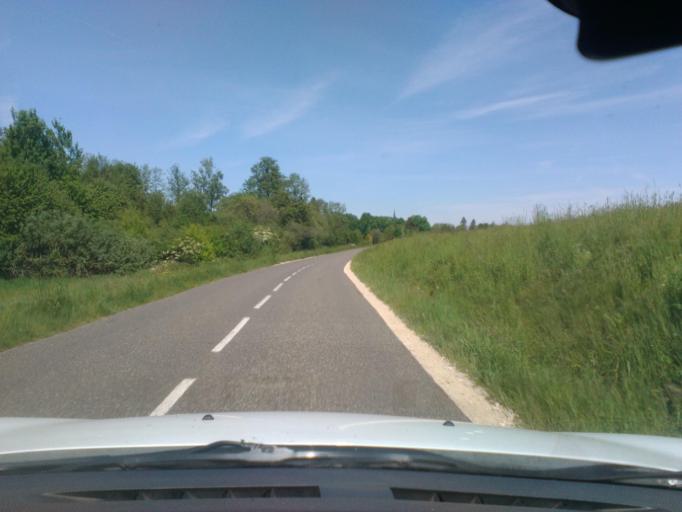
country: FR
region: Lorraine
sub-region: Departement des Vosges
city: Jeanmenil
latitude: 48.2897
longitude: 6.6936
